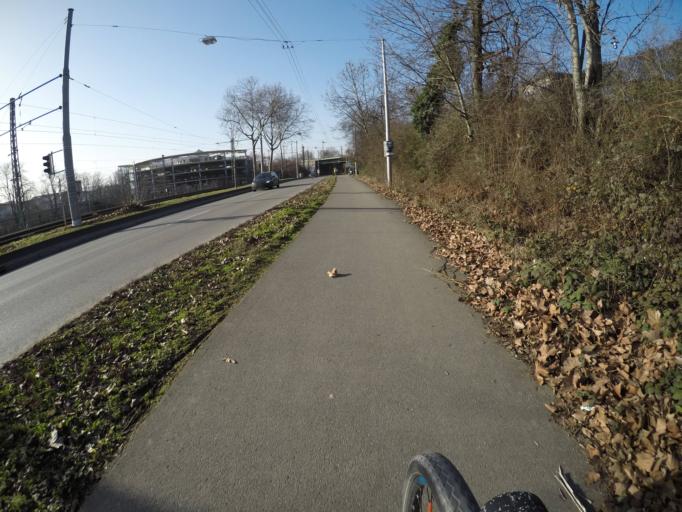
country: DE
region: Baden-Wuerttemberg
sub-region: Regierungsbezirk Stuttgart
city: Stuttgart-Ost
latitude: 48.7972
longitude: 9.2369
